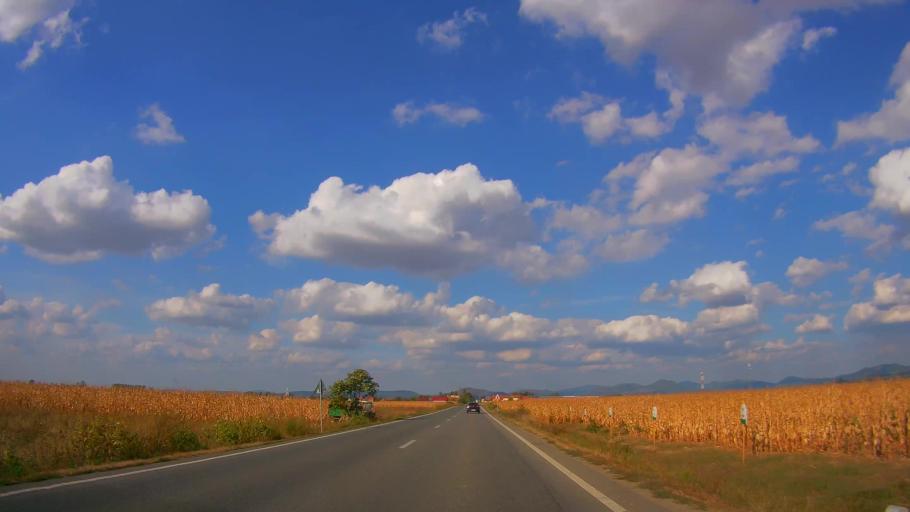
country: RO
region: Satu Mare
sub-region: Comuna Turulung
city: Turulung
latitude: 47.9197
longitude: 23.0823
